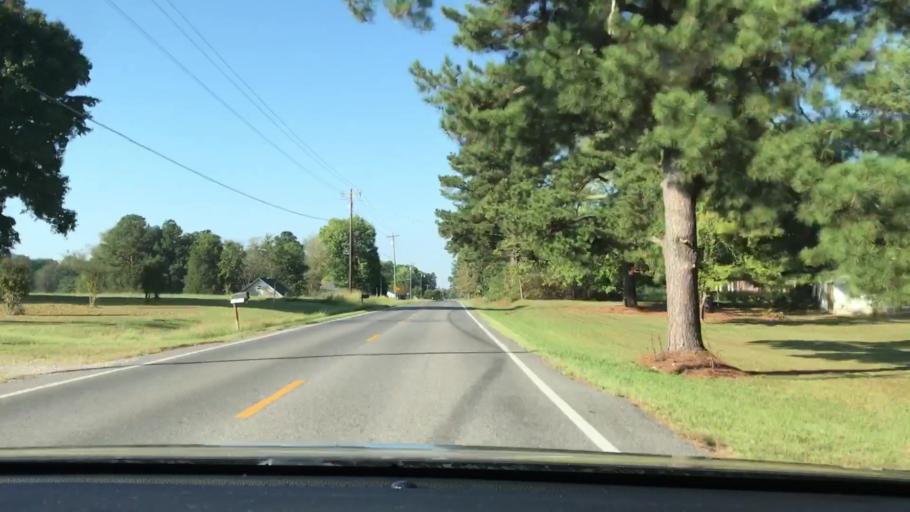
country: US
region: Kentucky
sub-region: Marshall County
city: Benton
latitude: 36.7713
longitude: -88.1710
